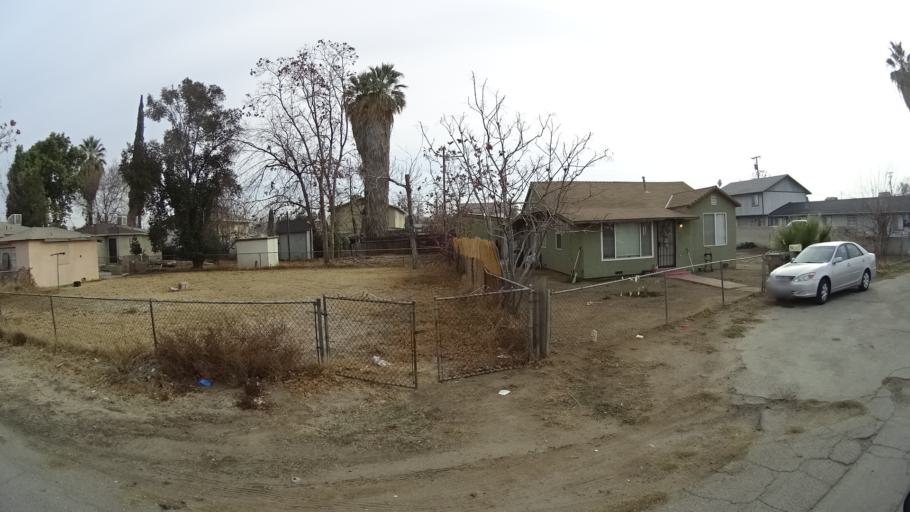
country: US
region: California
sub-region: Kern County
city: Bakersfield
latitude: 35.3565
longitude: -119.0178
